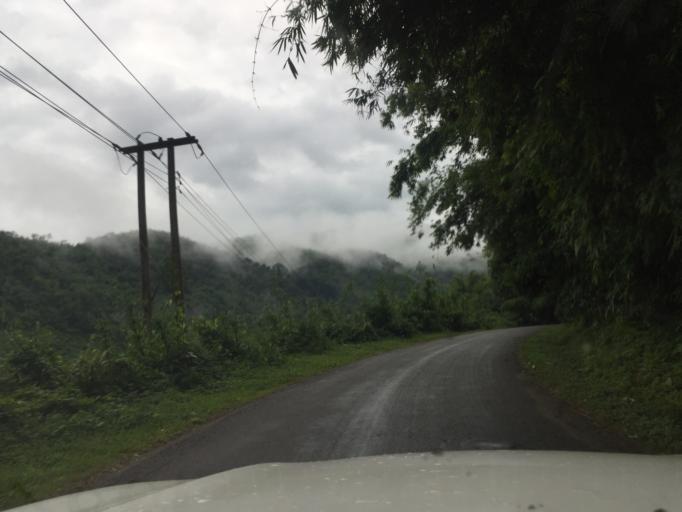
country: LA
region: Oudomxai
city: Muang La
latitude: 20.9023
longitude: 102.1805
